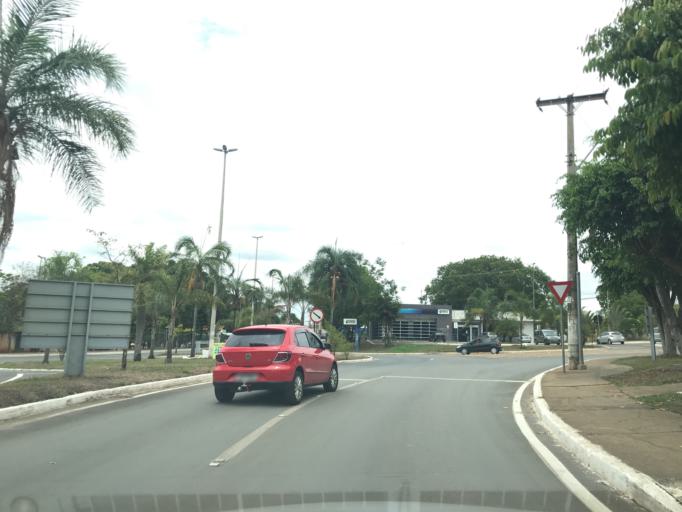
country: BR
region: Federal District
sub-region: Brasilia
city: Brasilia
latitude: -15.8543
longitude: -47.9499
